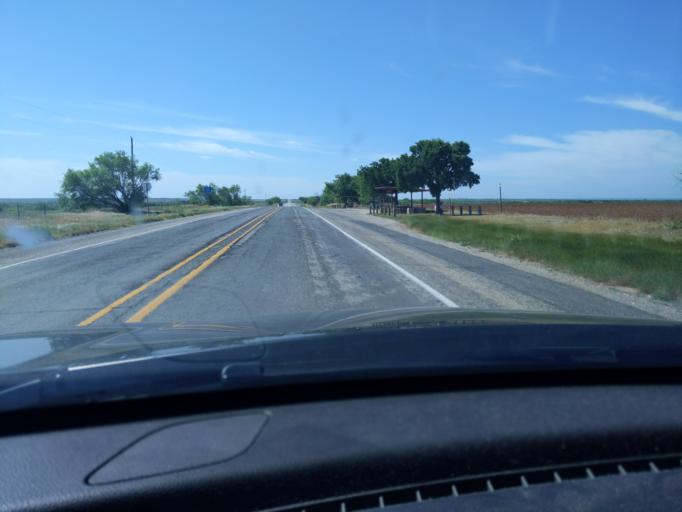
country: US
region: Texas
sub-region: Mitchell County
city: Colorado City
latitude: 32.3355
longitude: -100.8250
